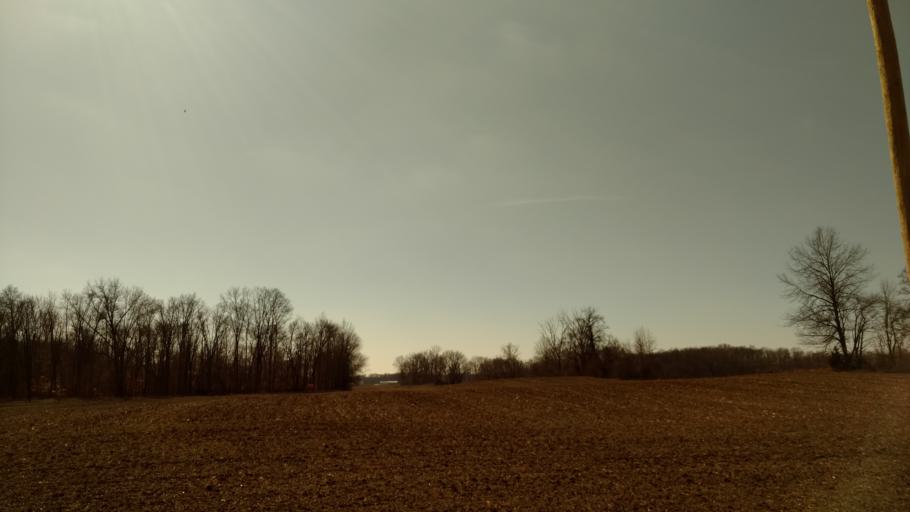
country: US
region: Ohio
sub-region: Morrow County
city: Mount Gilead
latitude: 40.5067
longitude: -82.7632
